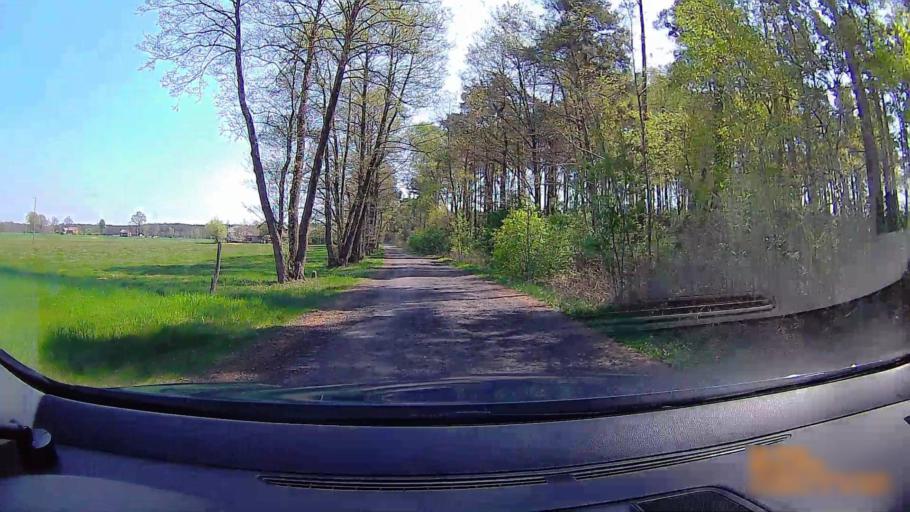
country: PL
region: Greater Poland Voivodeship
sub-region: Powiat koninski
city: Rychwal
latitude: 52.0926
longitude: 18.1776
